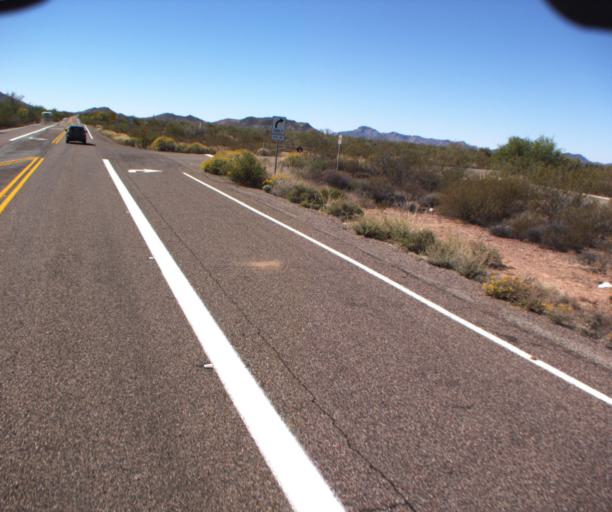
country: US
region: Arizona
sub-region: Pima County
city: Ajo
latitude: 32.1304
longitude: -112.7677
